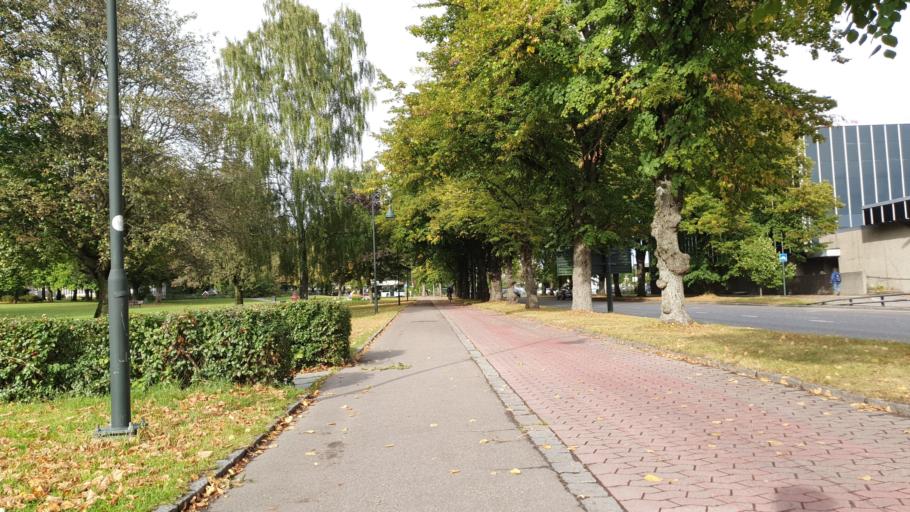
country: NO
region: Vestfold
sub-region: Tonsberg
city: Tonsberg
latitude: 59.2635
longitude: 10.4170
